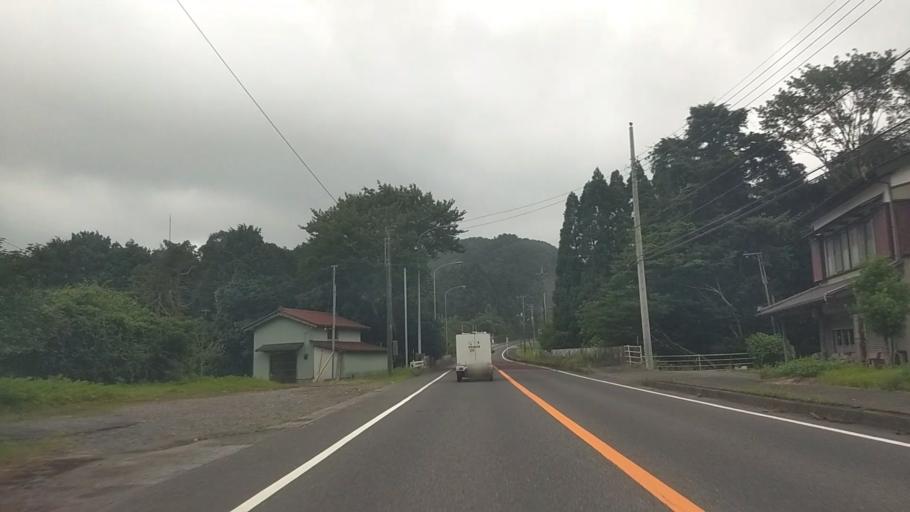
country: JP
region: Chiba
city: Kawaguchi
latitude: 35.1846
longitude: 140.0608
